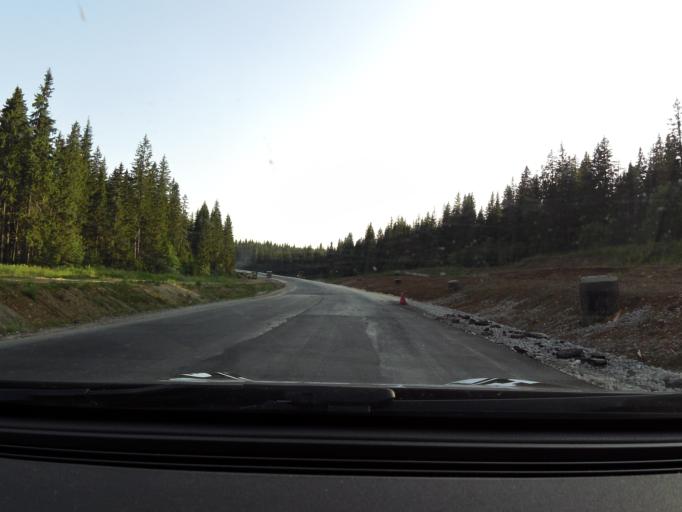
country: RU
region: Sverdlovsk
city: Nizhniye Sergi
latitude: 56.6700
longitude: 59.2713
